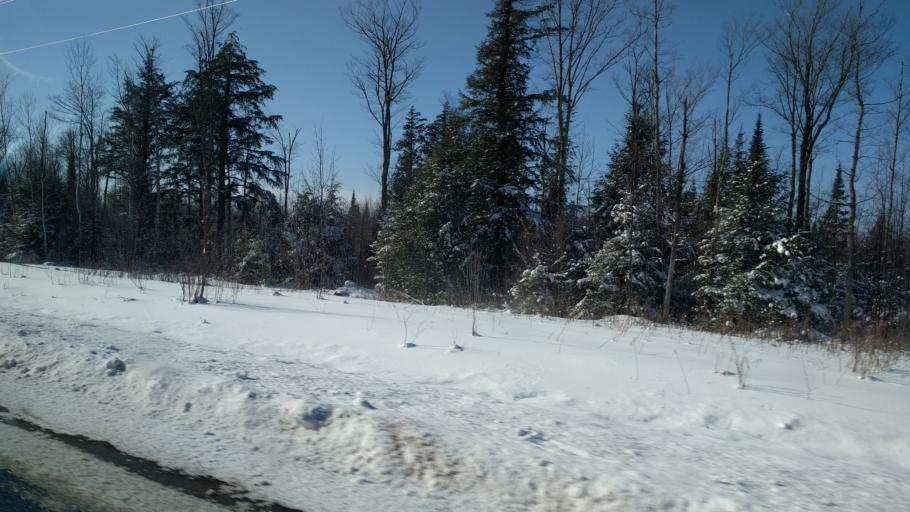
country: US
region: Wisconsin
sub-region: Iron County
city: Hurley
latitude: 46.3921
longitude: -90.3488
